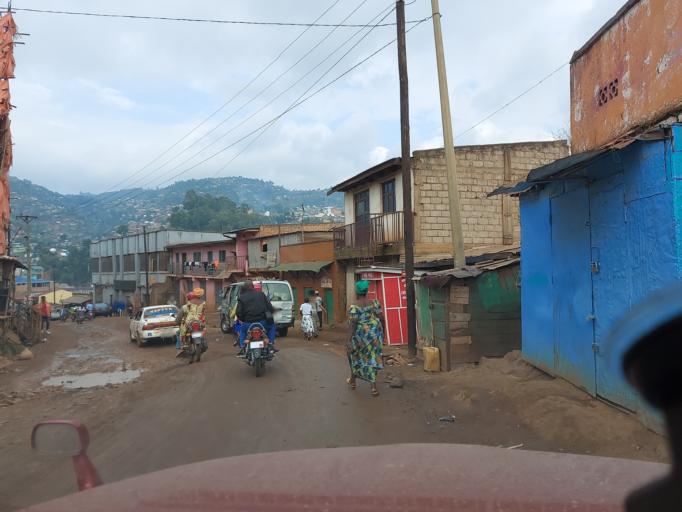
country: CD
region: South Kivu
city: Bukavu
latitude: -2.5224
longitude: 28.8540
